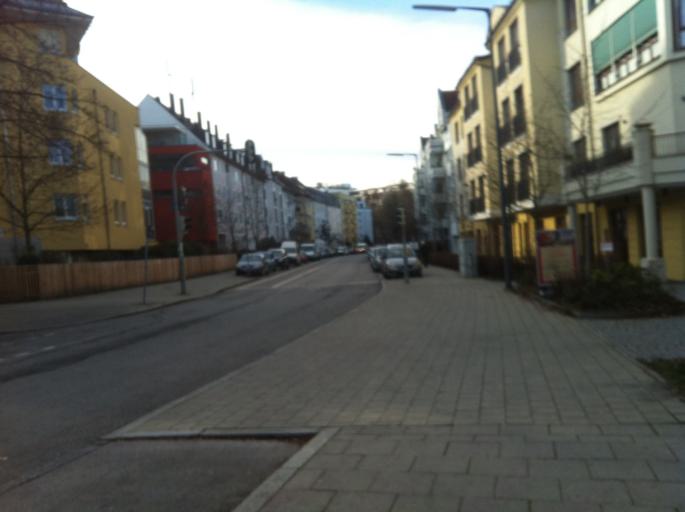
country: DE
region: Bavaria
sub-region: Upper Bavaria
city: Munich
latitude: 48.1051
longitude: 11.5435
